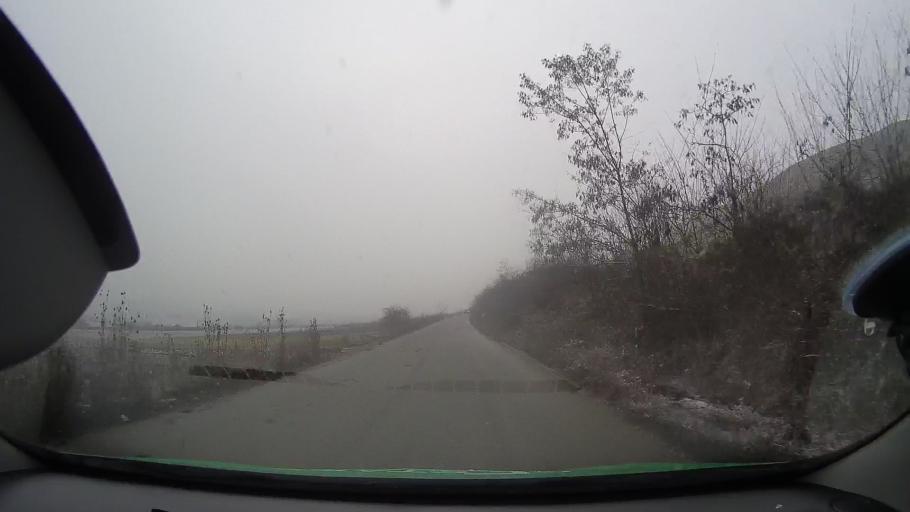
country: RO
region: Alba
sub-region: Comuna Noslac
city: Noslac
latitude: 46.3682
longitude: 23.9293
